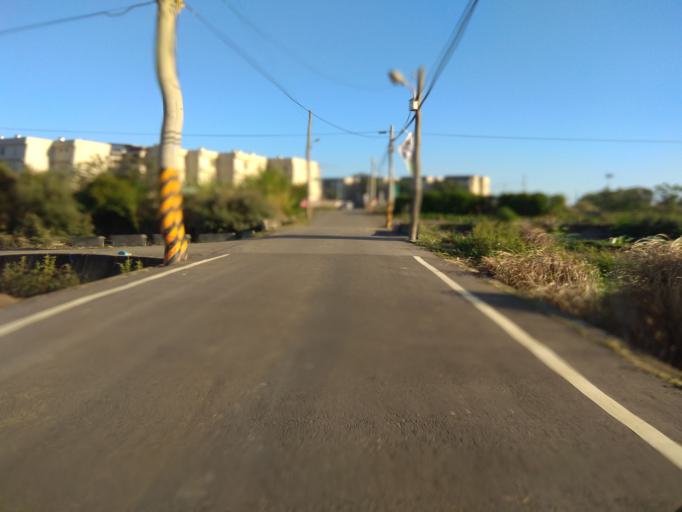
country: TW
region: Taiwan
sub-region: Hsinchu
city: Zhubei
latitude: 24.9907
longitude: 121.0516
